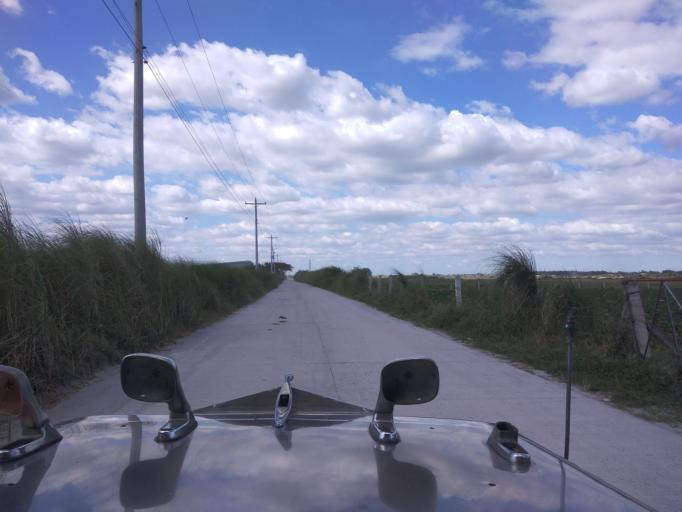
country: PH
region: Central Luzon
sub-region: Province of Pampanga
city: Magliman
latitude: 15.0445
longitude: 120.6287
